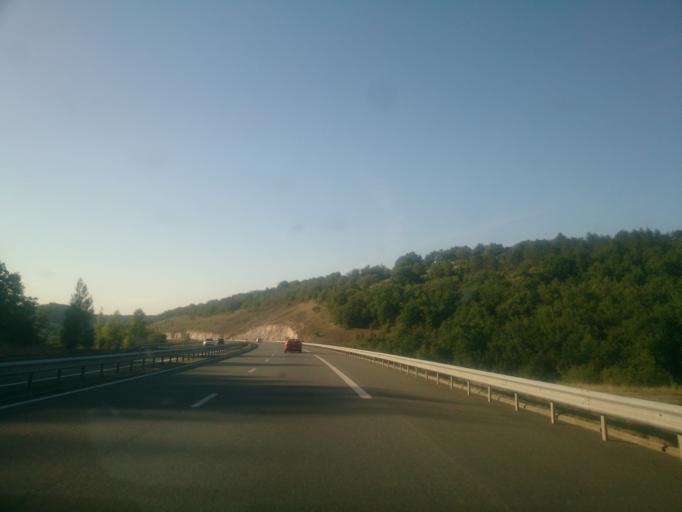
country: FR
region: Midi-Pyrenees
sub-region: Departement du Lot
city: Le Vigan
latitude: 44.7387
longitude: 1.5547
